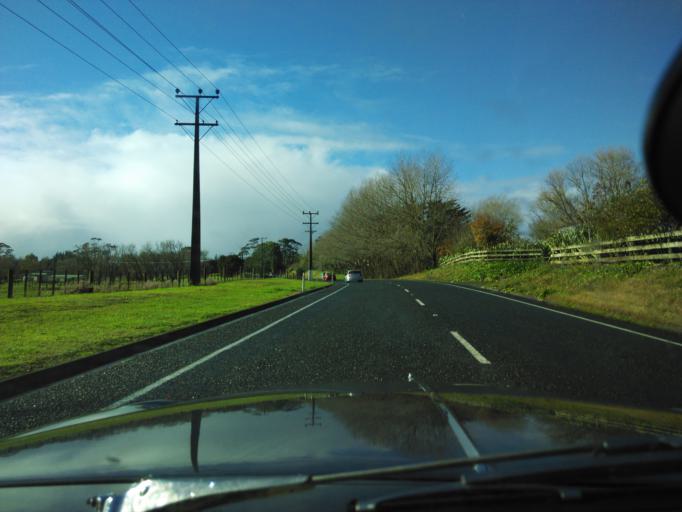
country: NZ
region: Auckland
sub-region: Auckland
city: Rothesay Bay
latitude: -36.6260
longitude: 174.6483
